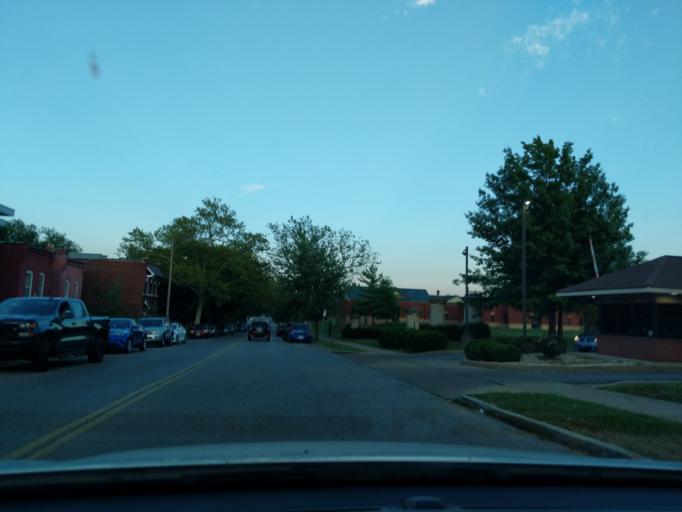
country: US
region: Missouri
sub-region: Saint Louis County
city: Maplewood
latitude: 38.6060
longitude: -90.2789
